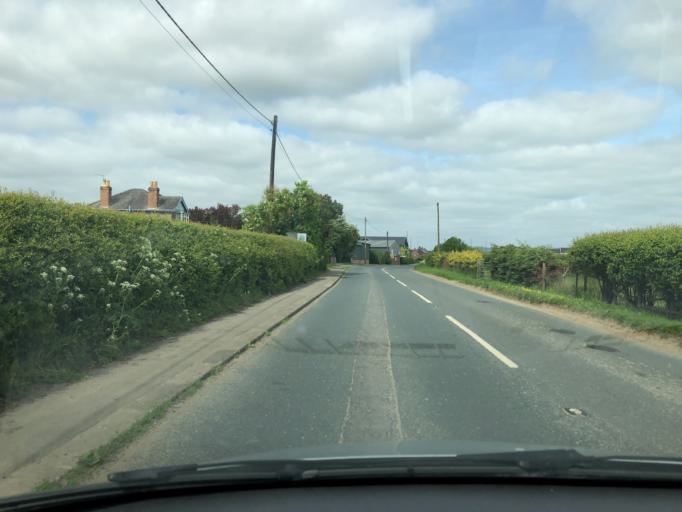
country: GB
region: England
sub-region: North Yorkshire
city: Thirsk
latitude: 54.2163
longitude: -1.3543
